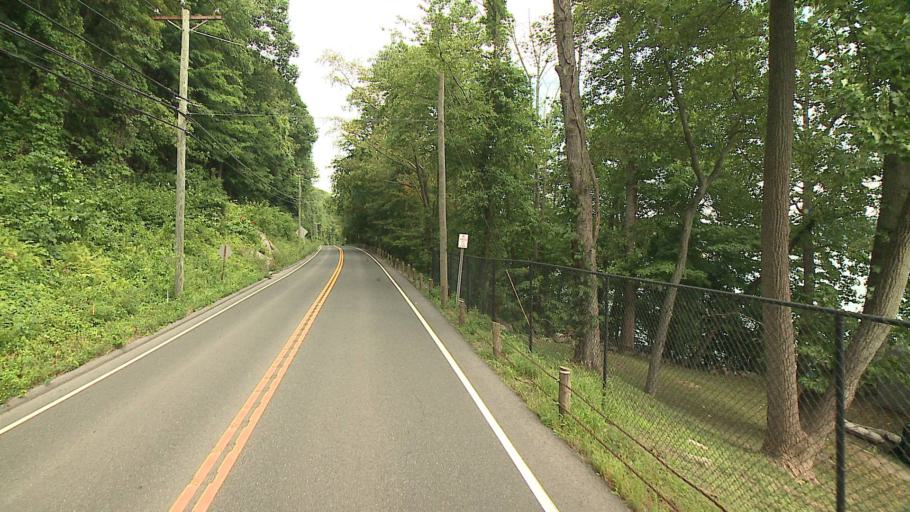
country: US
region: New York
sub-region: Putnam County
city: Putnam Lake
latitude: 41.4918
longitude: -73.4670
